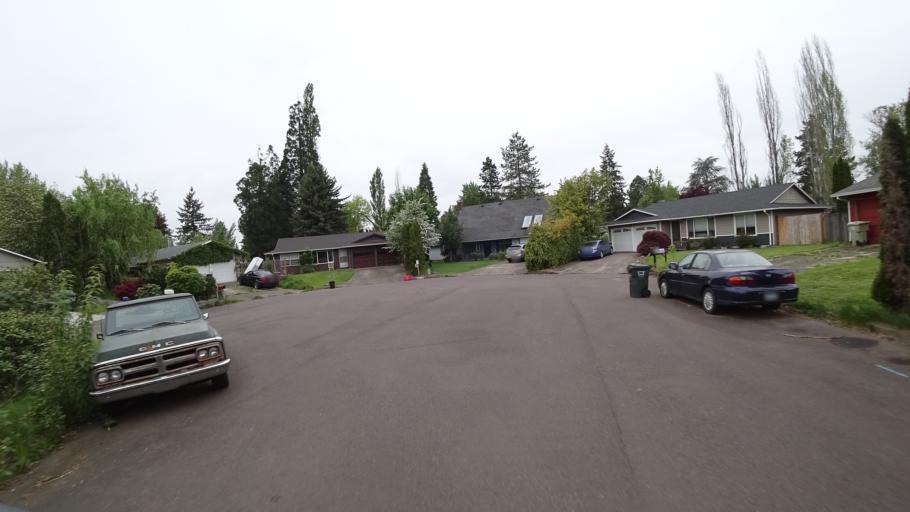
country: US
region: Oregon
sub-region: Washington County
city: Aloha
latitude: 45.5052
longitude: -122.8783
